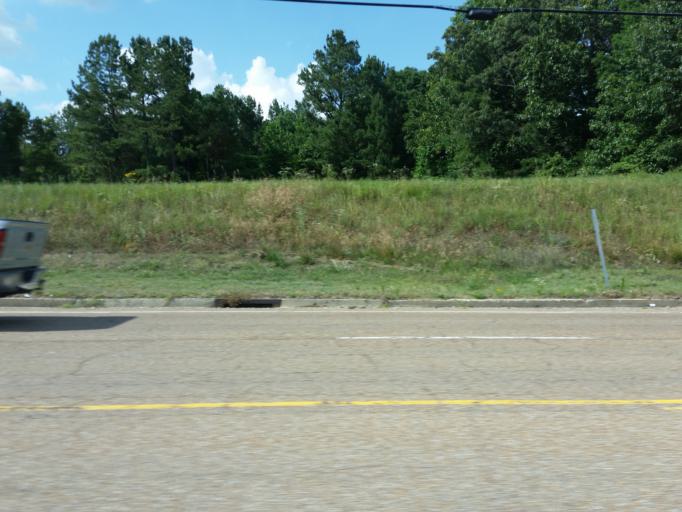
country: US
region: Tennessee
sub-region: Henderson County
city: Lexington
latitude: 35.6392
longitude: -88.3597
